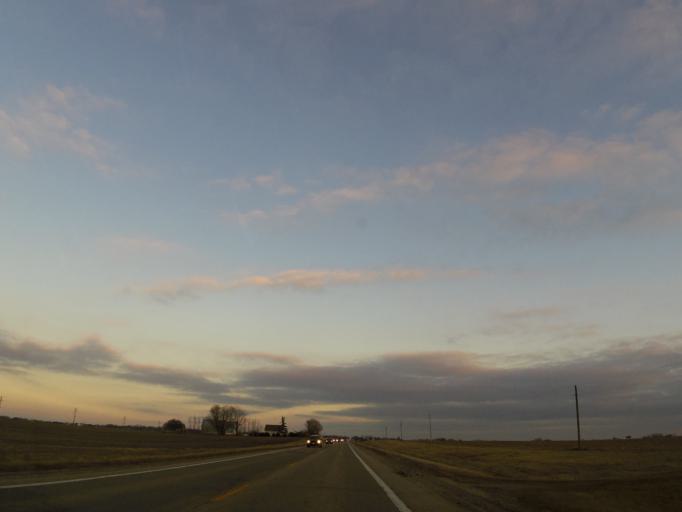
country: US
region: Illinois
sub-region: McLean County
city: Gridley
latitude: 40.7393
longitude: -88.9101
